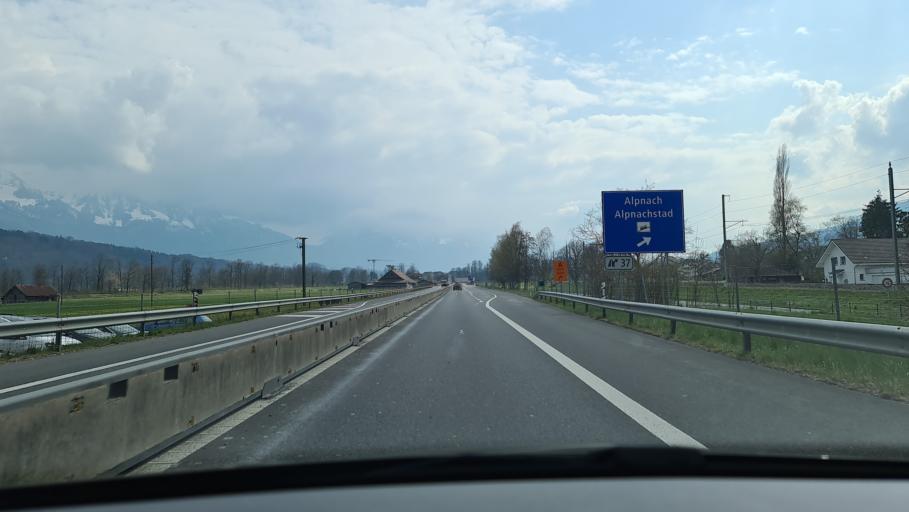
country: CH
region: Obwalden
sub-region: Obwalden
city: Alpnach
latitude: 46.9530
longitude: 8.2778
